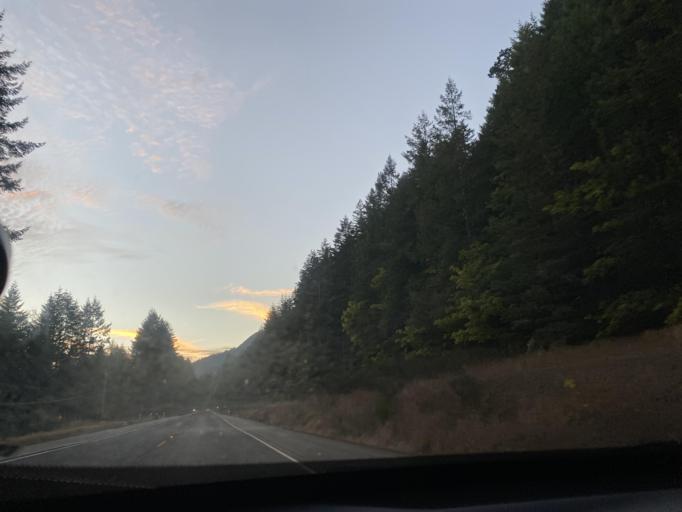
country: US
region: Washington
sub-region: Clallam County
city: Port Angeles
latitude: 48.0862
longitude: -123.7161
